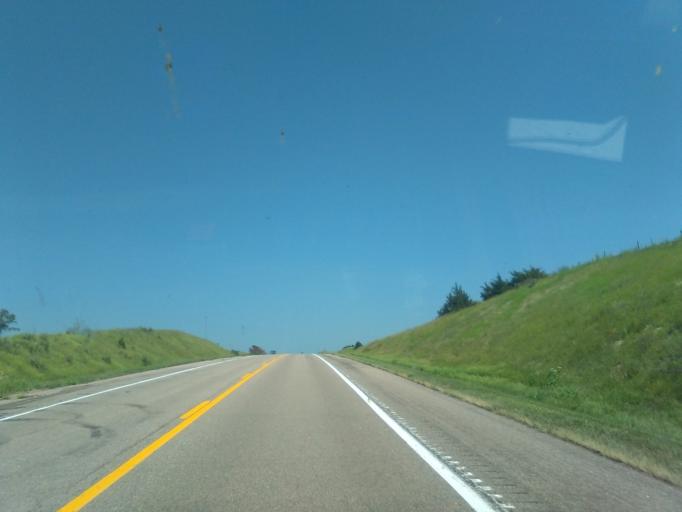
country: US
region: Nebraska
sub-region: Frontier County
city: Stockville
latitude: 40.5873
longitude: -100.6295
